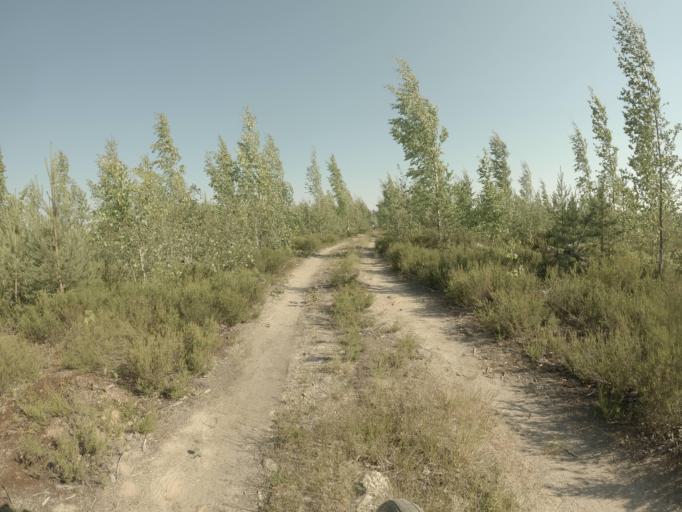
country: RU
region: Leningrad
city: Yakovlevo
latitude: 60.4431
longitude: 29.2406
